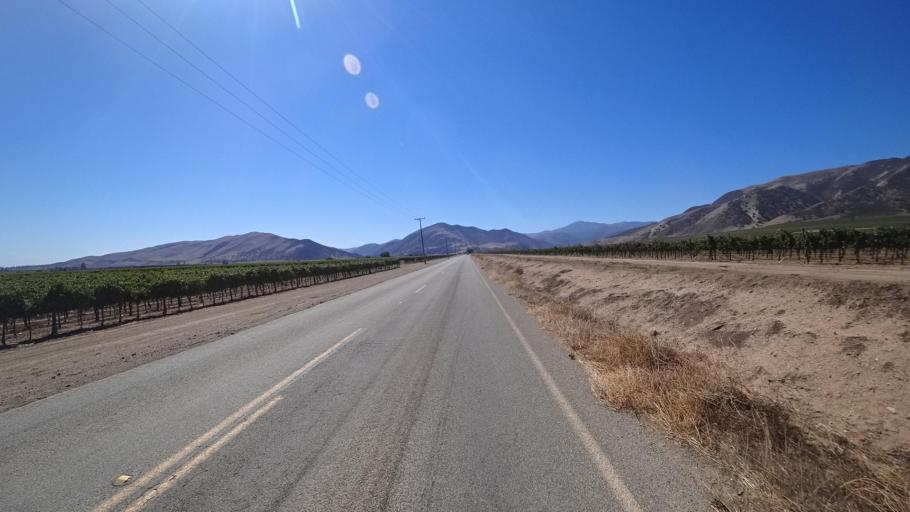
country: US
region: California
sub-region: Monterey County
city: Greenfield
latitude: 36.3109
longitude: -121.3152
